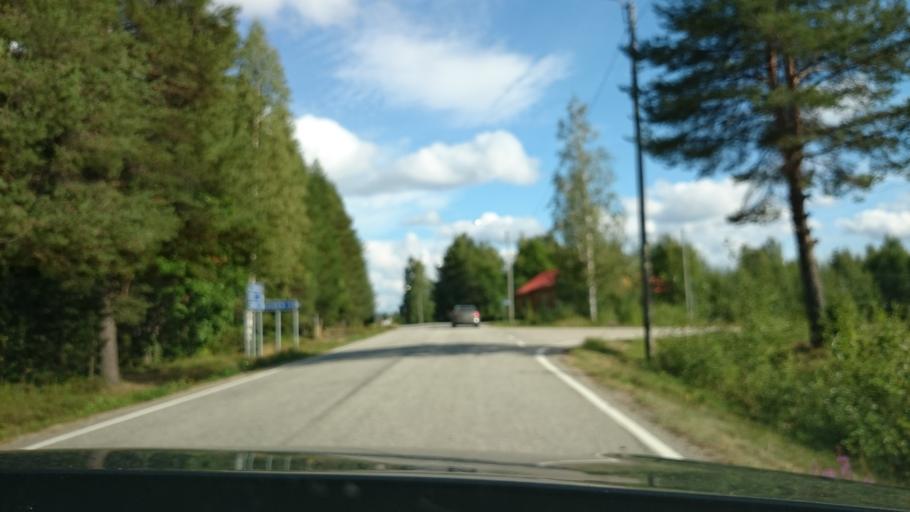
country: FI
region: Kainuu
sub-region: Kehys-Kainuu
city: Suomussalmi
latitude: 64.7473
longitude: 29.4399
